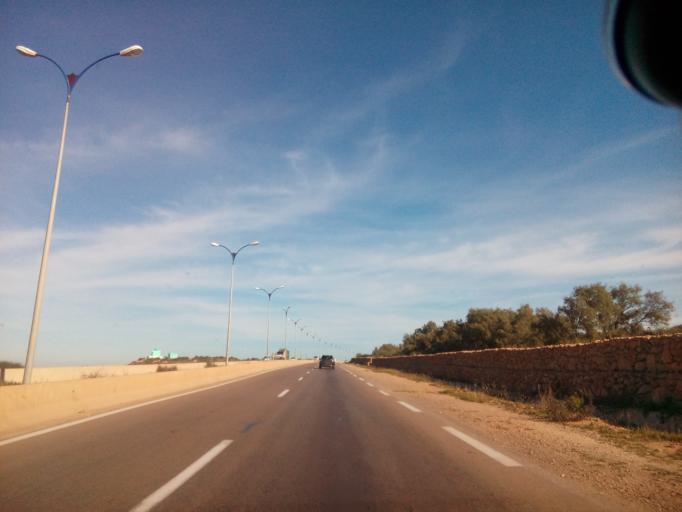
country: DZ
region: Oran
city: Ain el Bya
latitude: 35.7909
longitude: -0.0943
